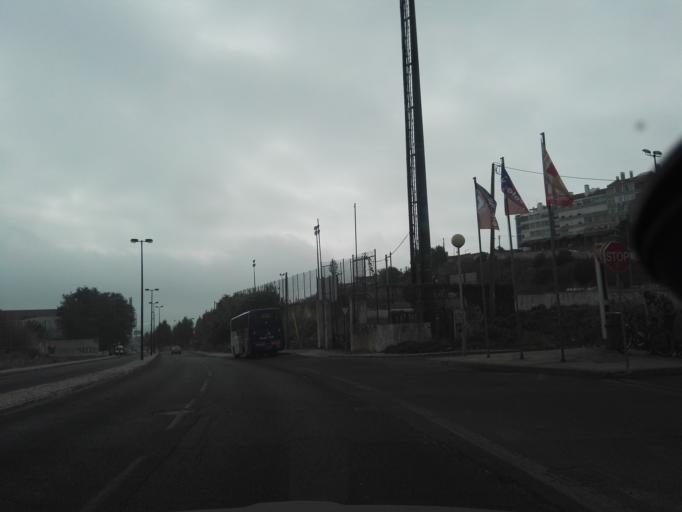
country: PT
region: Lisbon
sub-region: Lisbon
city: Lisbon
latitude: 38.7227
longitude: -9.1213
